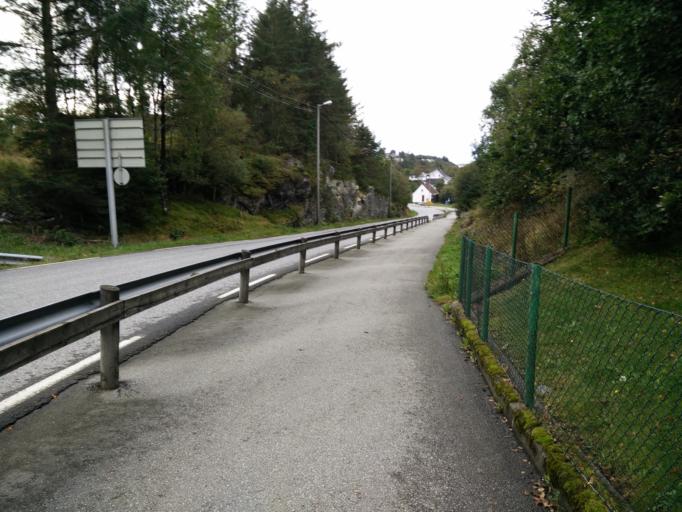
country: NO
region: Hordaland
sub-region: Sveio
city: Sveio
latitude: 59.6043
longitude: 5.2117
